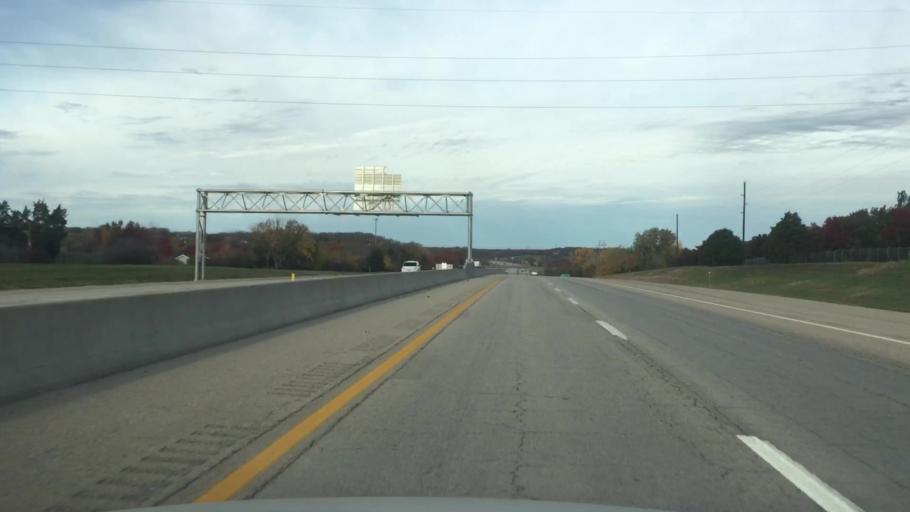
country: US
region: Kansas
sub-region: Douglas County
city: Lawrence
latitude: 38.9925
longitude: -95.2693
